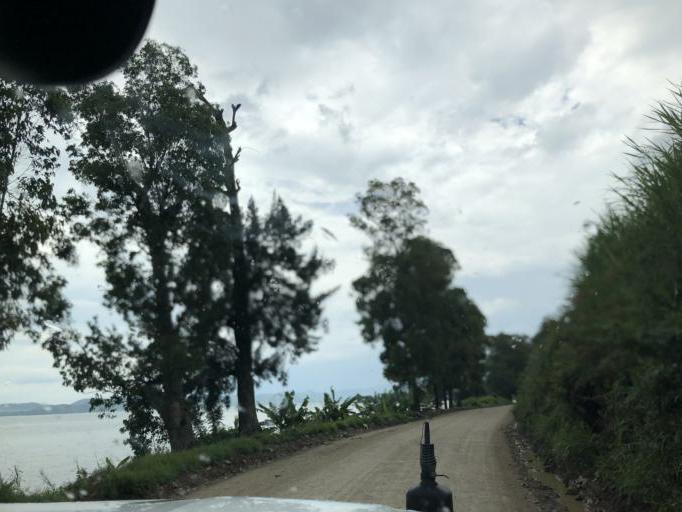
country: CD
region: Nord Kivu
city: Sake
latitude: -1.5949
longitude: 29.0403
